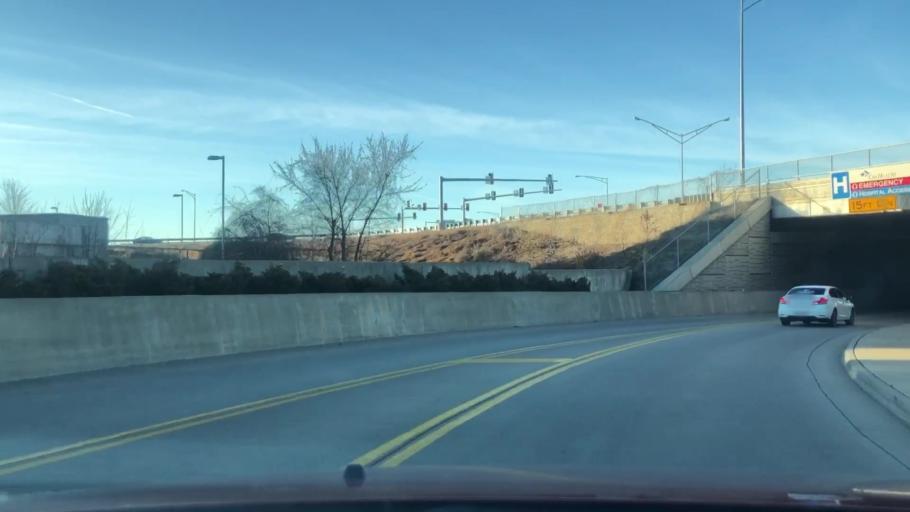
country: US
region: Missouri
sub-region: Greene County
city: Springfield
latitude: 37.1441
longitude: -93.2776
